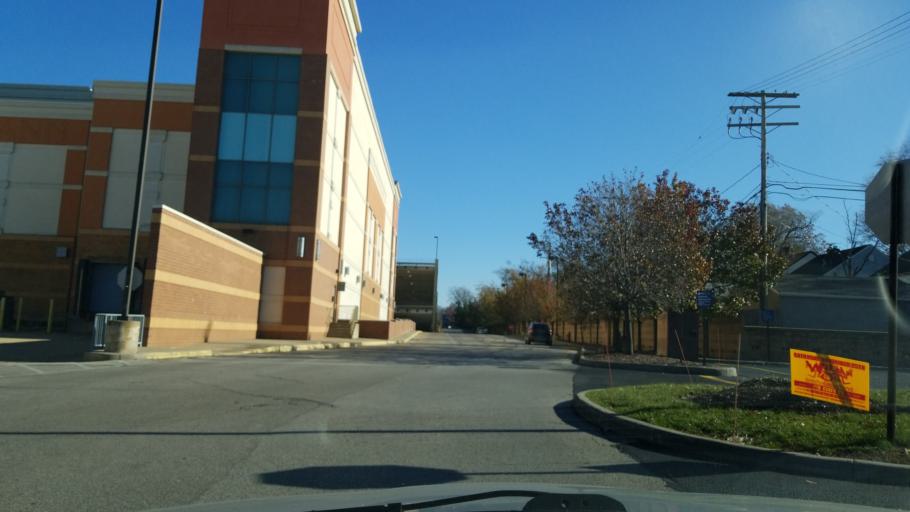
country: US
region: Ohio
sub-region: Cuyahoga County
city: University Heights
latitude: 41.4993
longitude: -81.5358
